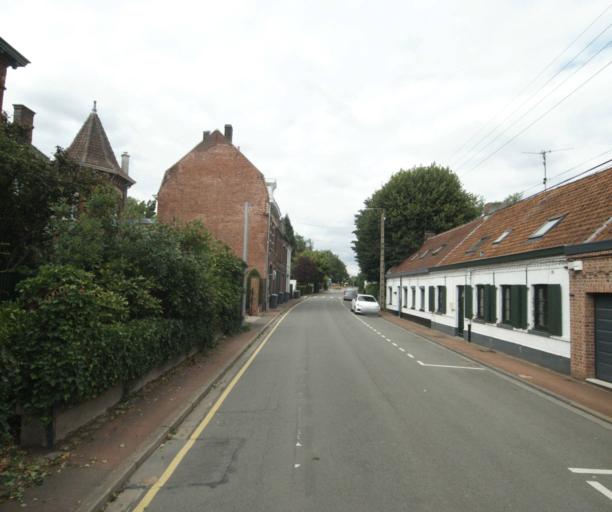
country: FR
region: Nord-Pas-de-Calais
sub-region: Departement du Nord
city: Hem
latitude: 50.6549
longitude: 3.1729
